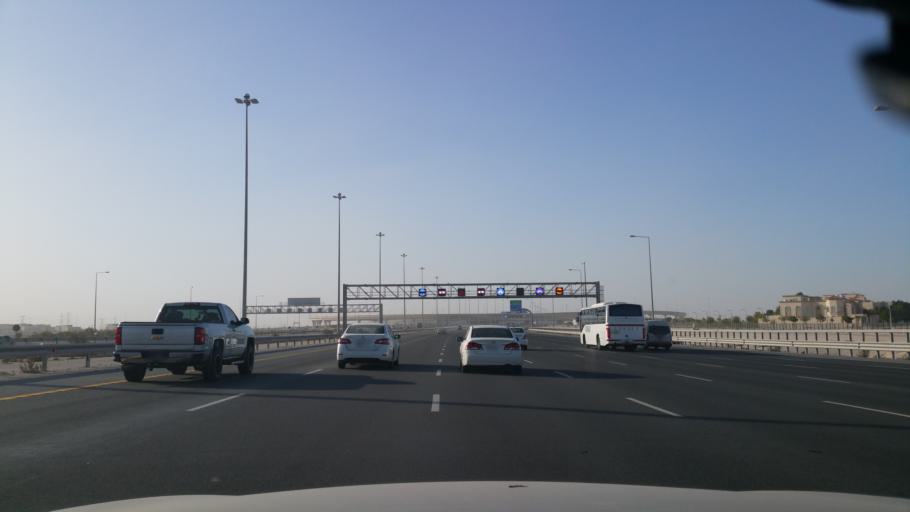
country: QA
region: Al Wakrah
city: Al Wukayr
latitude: 25.1756
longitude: 51.5542
